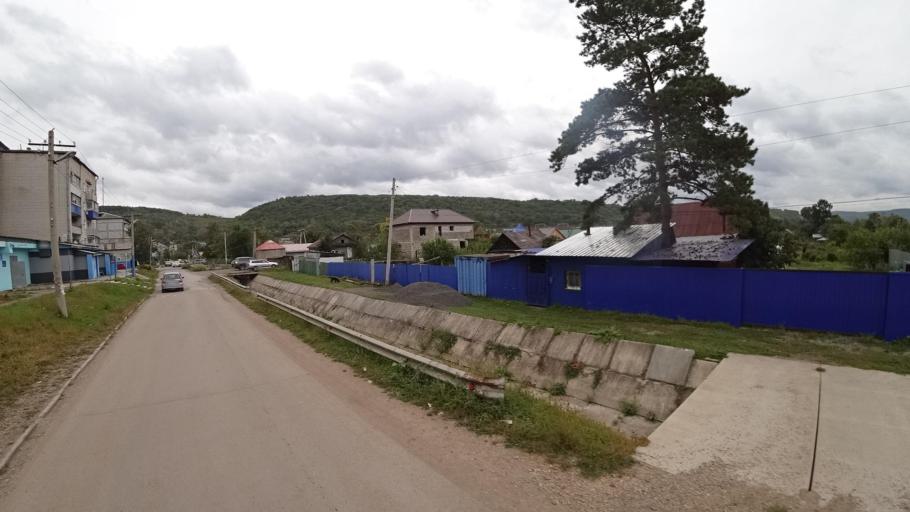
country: RU
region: Jewish Autonomous Oblast
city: Khingansk
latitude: 49.0086
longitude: 131.0516
